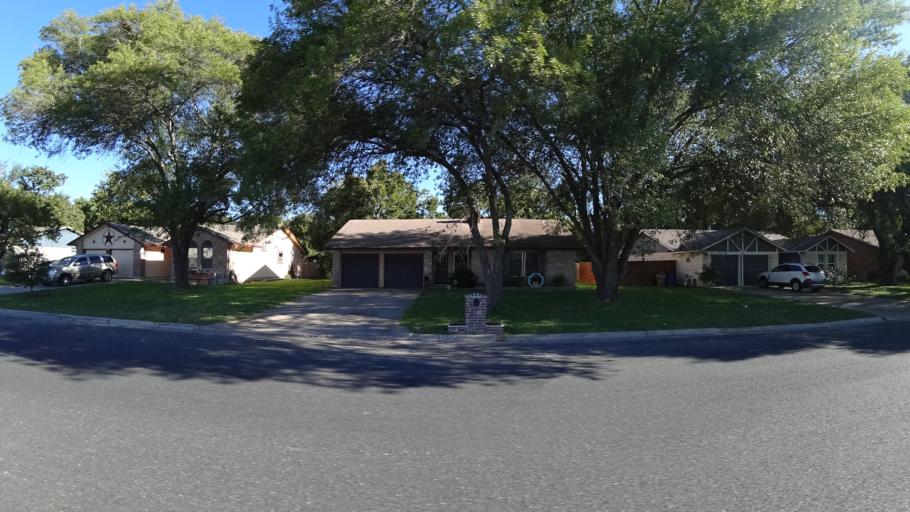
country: US
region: Texas
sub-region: Travis County
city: Hornsby Bend
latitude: 30.3139
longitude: -97.6546
